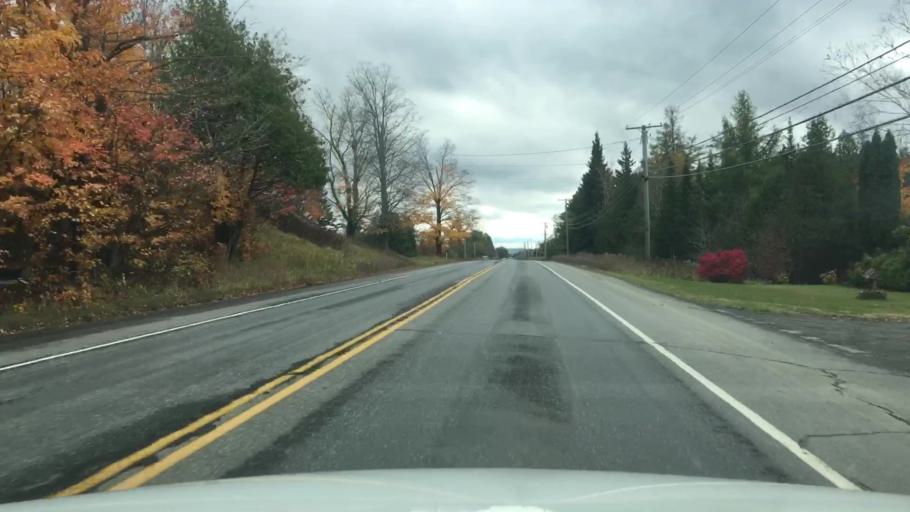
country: US
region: Maine
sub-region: Aroostook County
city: Houlton
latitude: 46.1920
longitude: -67.8414
